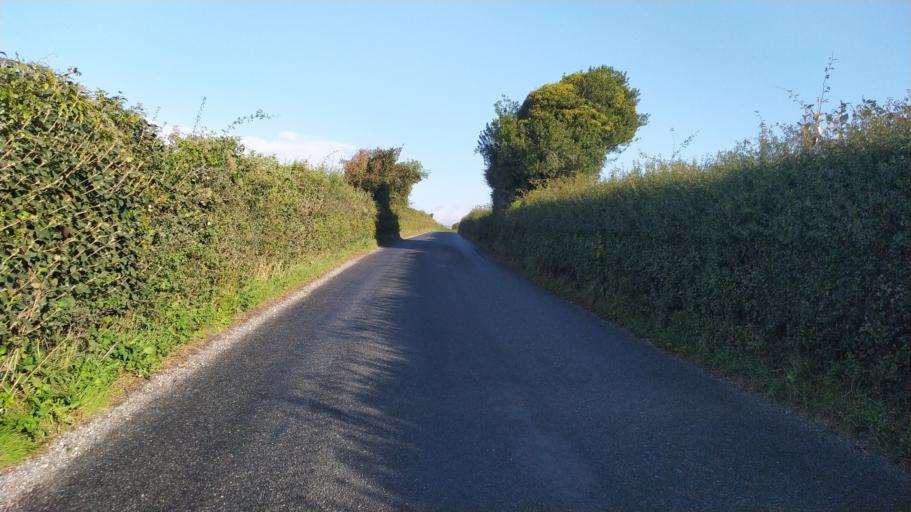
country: GB
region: England
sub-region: Wiltshire
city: Ansty
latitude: 50.9204
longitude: -2.0537
